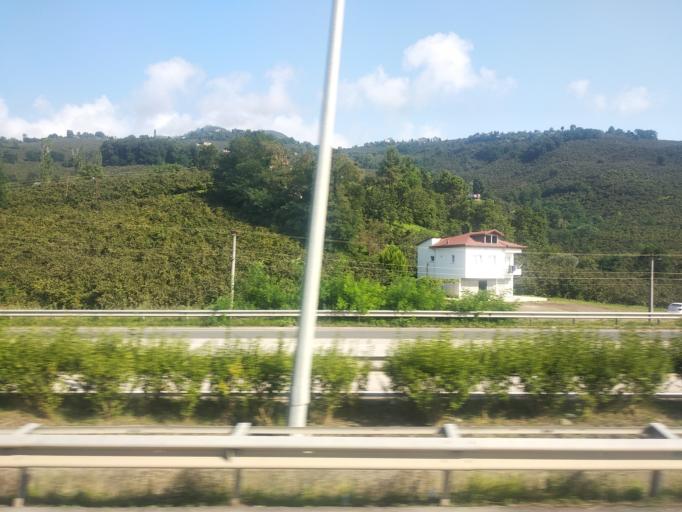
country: TR
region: Ordu
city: Ordu
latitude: 41.0081
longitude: 37.8301
